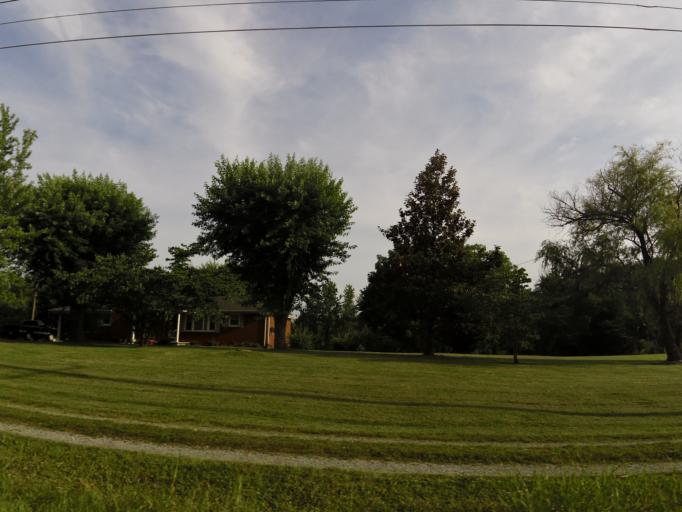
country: US
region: Tennessee
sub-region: Dickson County
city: Dickson
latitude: 36.0864
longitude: -87.4145
